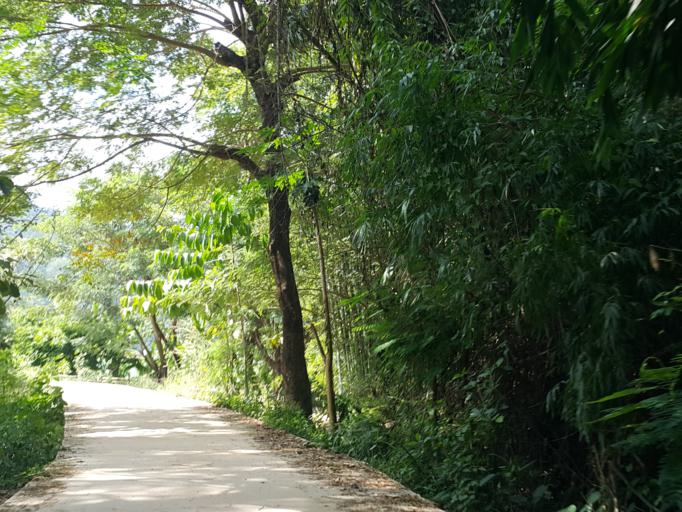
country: TH
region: Lampang
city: Chae Hom
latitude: 18.5647
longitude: 99.4515
